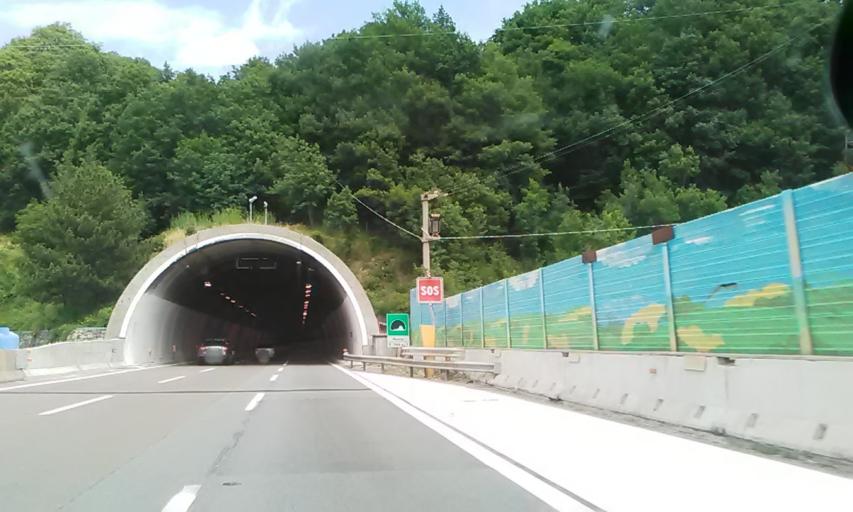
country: IT
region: Liguria
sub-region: Provincia di Genova
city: Rossiglione
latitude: 44.5685
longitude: 8.6614
